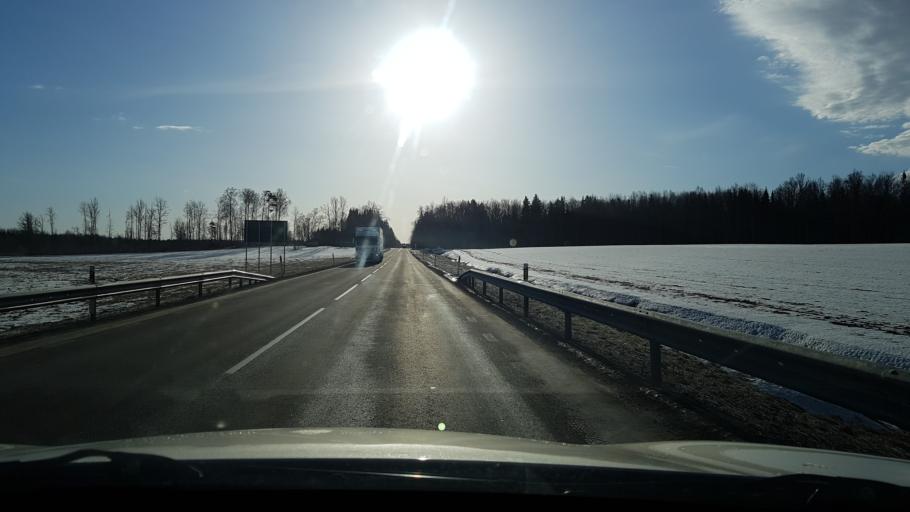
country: EE
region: Viljandimaa
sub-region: Vohma linn
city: Vohma
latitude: 58.5643
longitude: 25.5782
